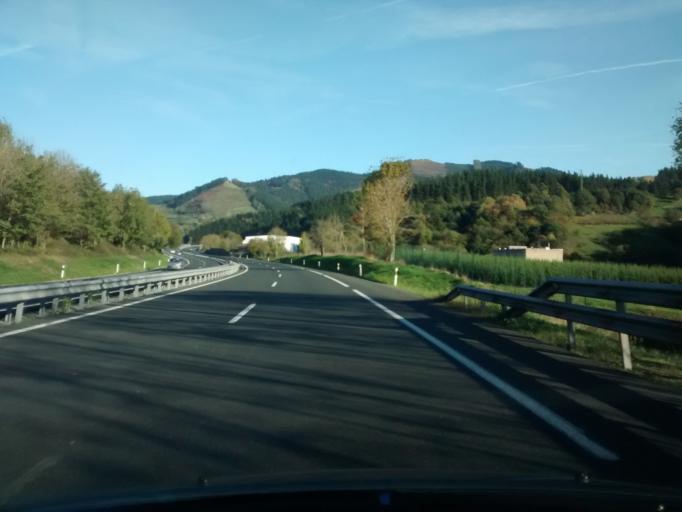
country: ES
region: Basque Country
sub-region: Bizkaia
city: Berriz
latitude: 43.1674
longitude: -2.5614
